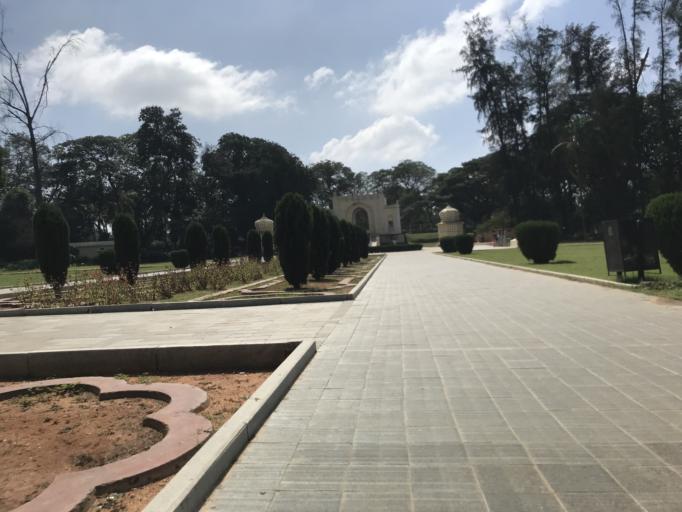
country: IN
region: Karnataka
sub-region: Mandya
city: Shrirangapattana
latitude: 12.4191
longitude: 76.6967
